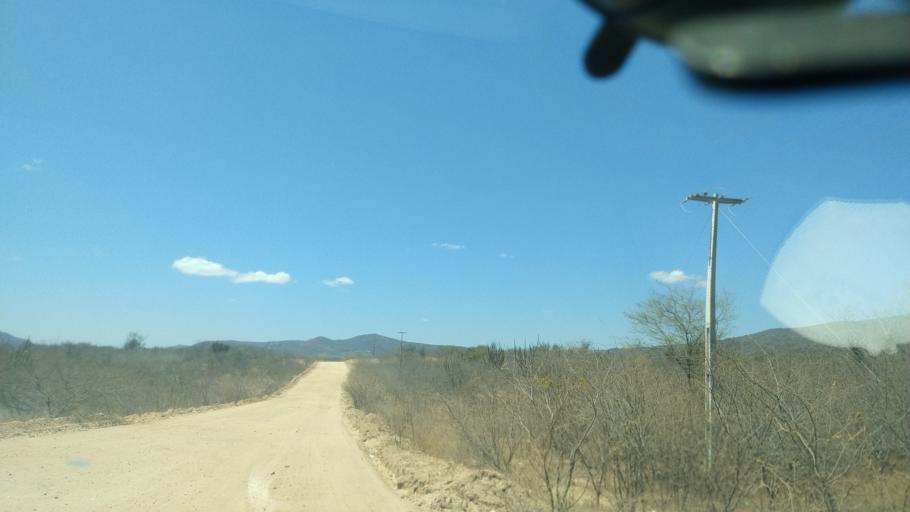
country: BR
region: Rio Grande do Norte
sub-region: Sao Tome
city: Sao Tome
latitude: -5.9741
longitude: -36.1675
